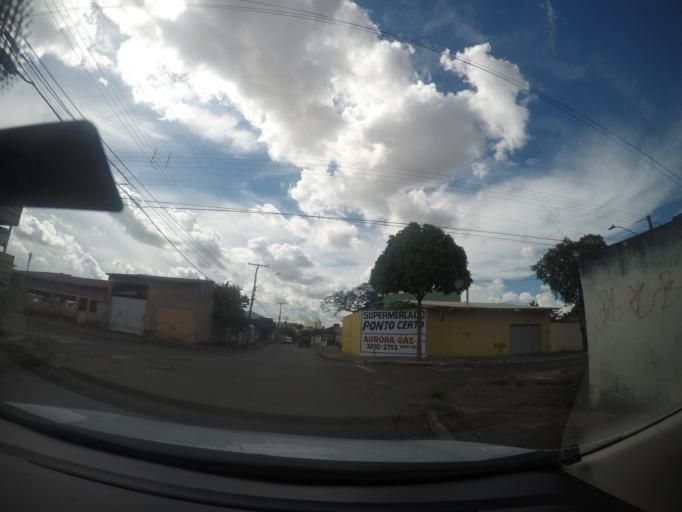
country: BR
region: Goias
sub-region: Goiania
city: Goiania
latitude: -16.6779
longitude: -49.3005
